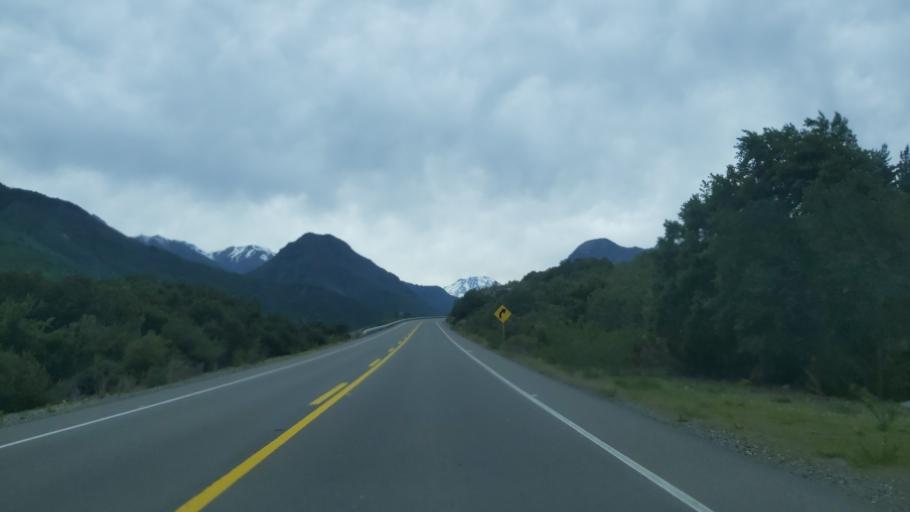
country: CL
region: Maule
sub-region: Provincia de Linares
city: Colbun
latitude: -35.7085
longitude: -71.1043
